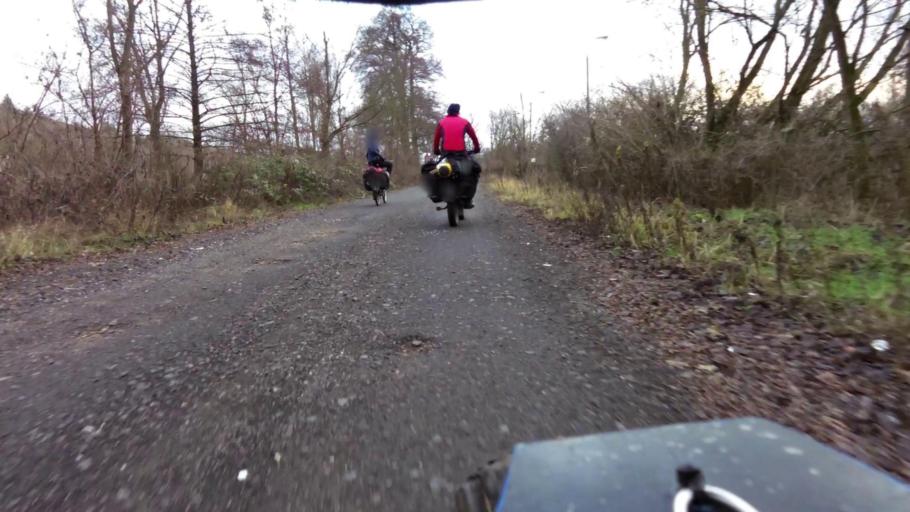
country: PL
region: Lubusz
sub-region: Powiat gorzowski
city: Jenin
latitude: 52.7099
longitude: 15.1311
